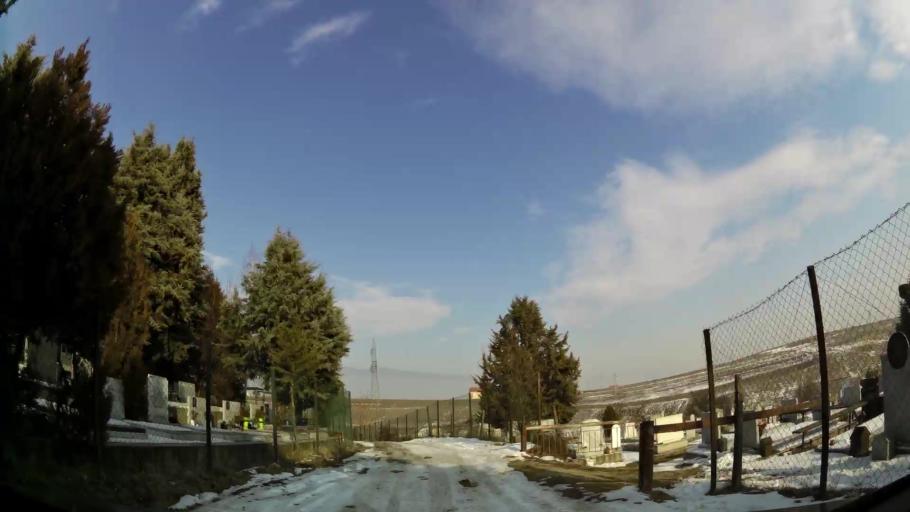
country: MK
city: Creshevo
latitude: 42.0163
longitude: 21.4943
